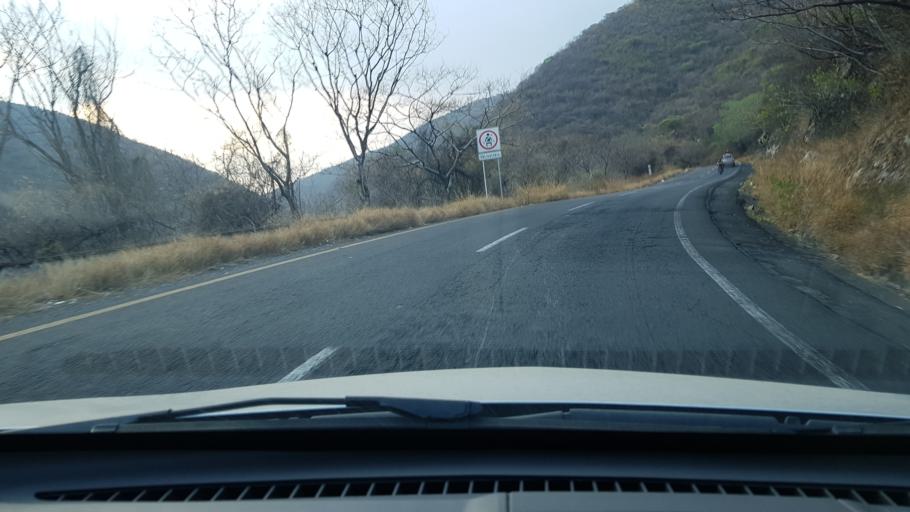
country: MX
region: Morelos
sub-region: Jiutepec
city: Independencia
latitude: 18.8585
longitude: -99.1172
